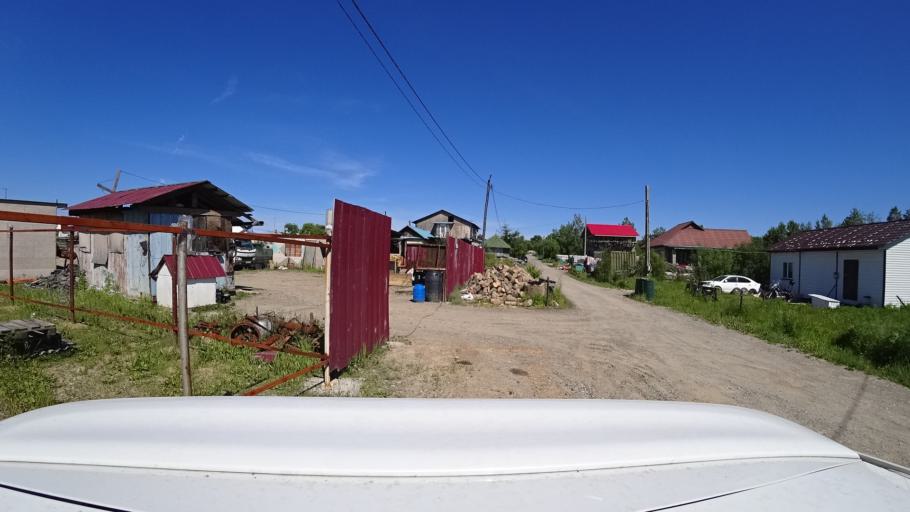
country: RU
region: Khabarovsk Krai
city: Topolevo
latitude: 48.5563
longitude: 135.1859
